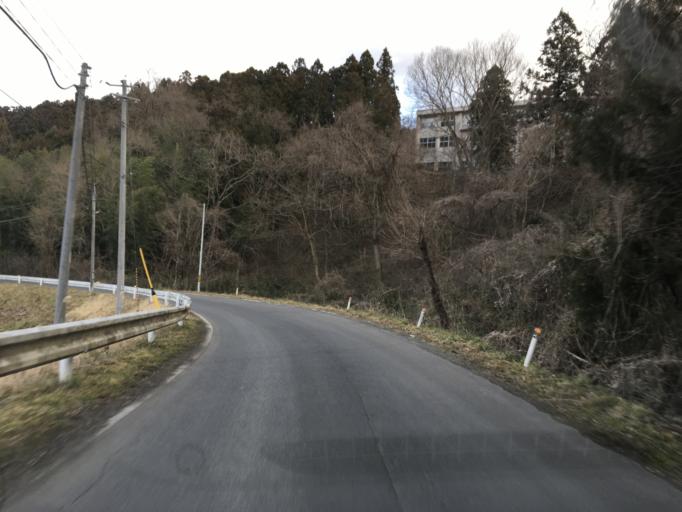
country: JP
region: Miyagi
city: Wakuya
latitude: 38.7126
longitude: 141.2956
